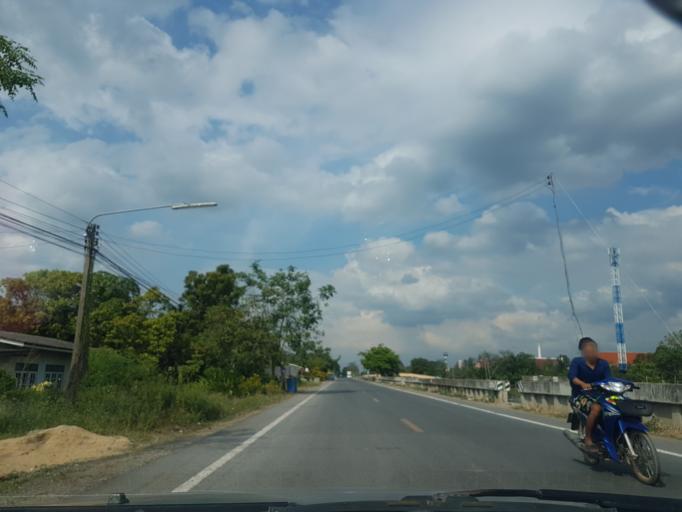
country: TH
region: Pathum Thani
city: Nong Suea
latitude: 14.1749
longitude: 100.8915
